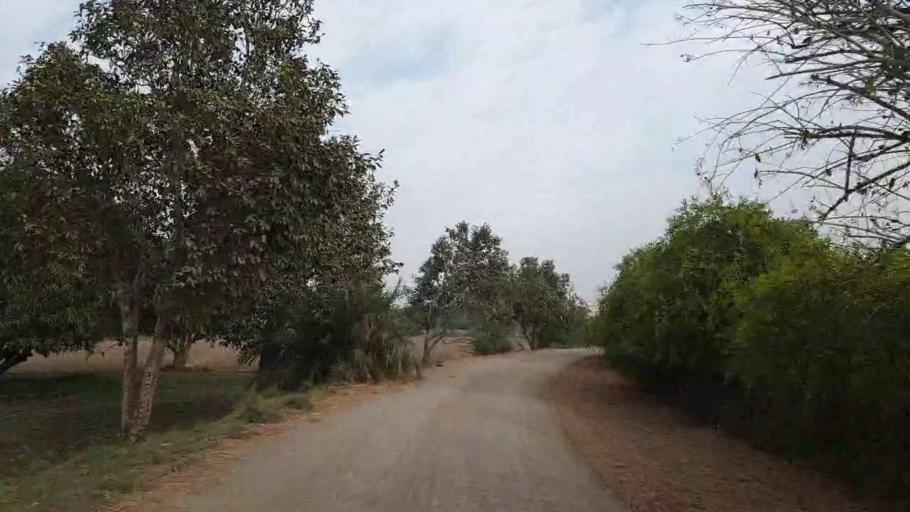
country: PK
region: Sindh
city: Tando Muhammad Khan
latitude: 25.0930
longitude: 68.4178
